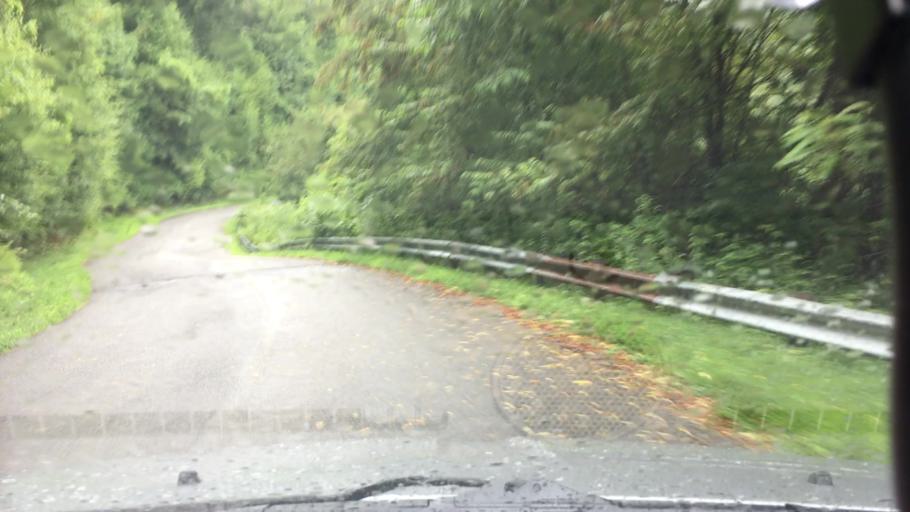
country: US
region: North Carolina
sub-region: Madison County
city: Mars Hill
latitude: 35.9504
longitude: -82.5145
